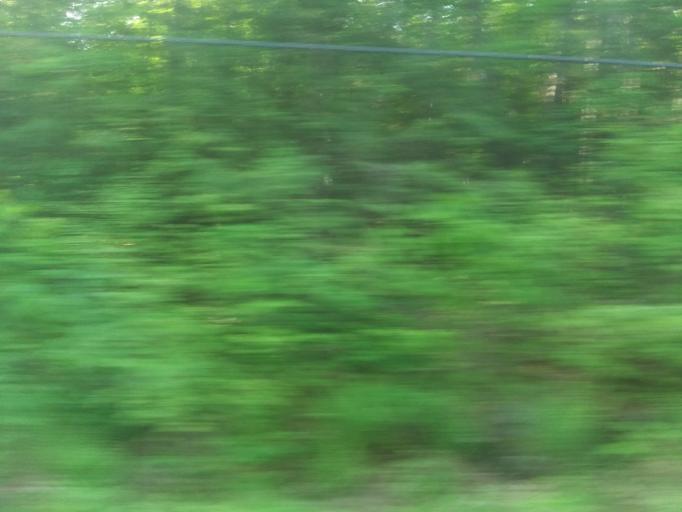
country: US
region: Massachusetts
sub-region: Franklin County
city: Shelburne Falls
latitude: 42.5835
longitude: -72.7488
